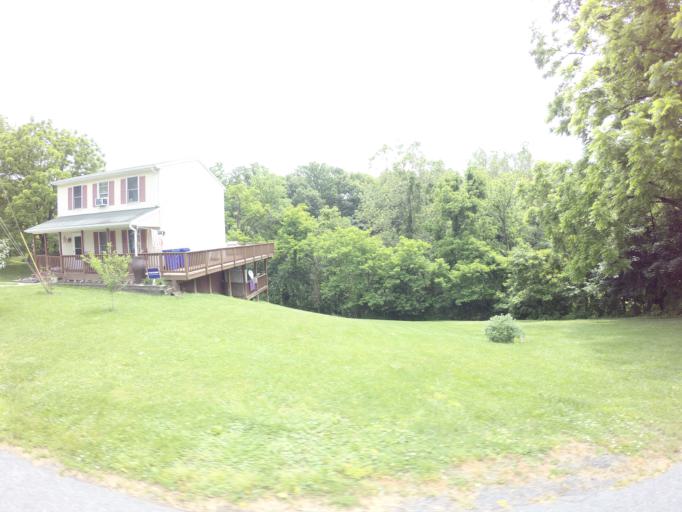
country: US
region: Maryland
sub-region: Frederick County
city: Brunswick
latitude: 39.3164
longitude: -77.6225
